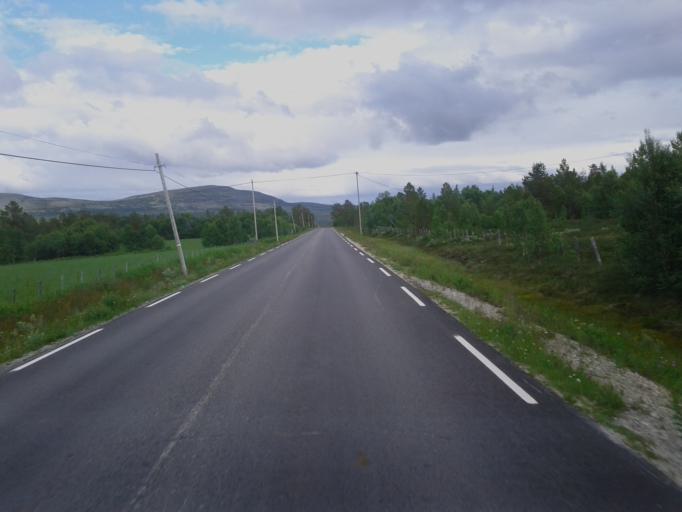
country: NO
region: Sor-Trondelag
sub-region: Roros
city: Roros
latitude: 62.3062
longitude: 11.6982
